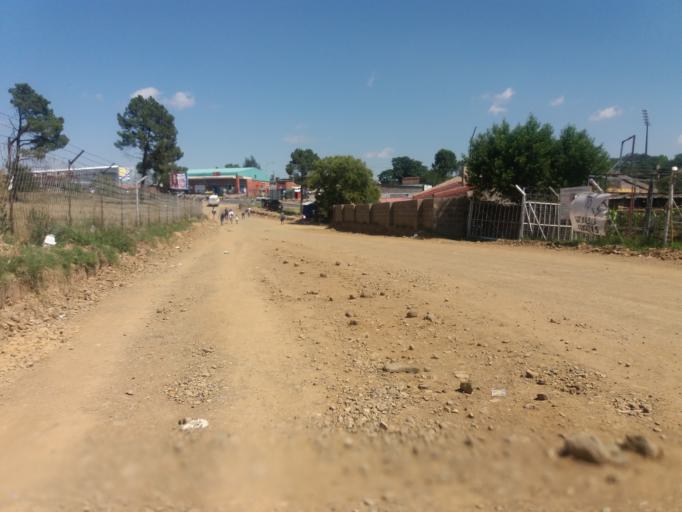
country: LS
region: Maseru
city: Maseru
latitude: -29.3153
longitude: 27.5031
